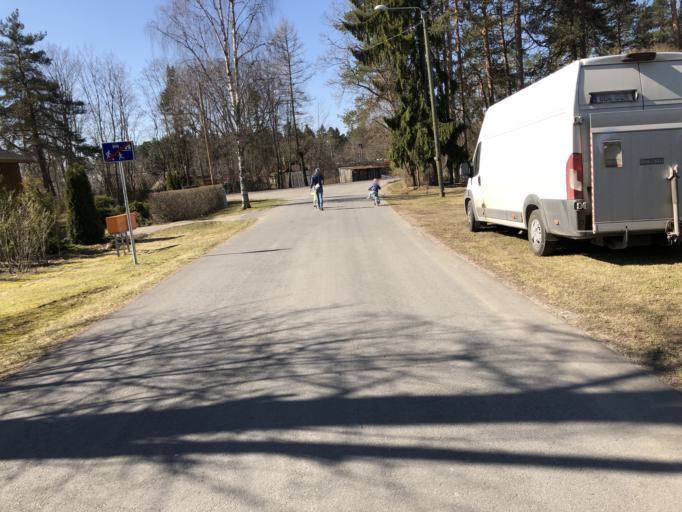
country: EE
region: Harju
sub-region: Kuusalu vald
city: Kuusalu
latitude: 59.2858
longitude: 25.6151
